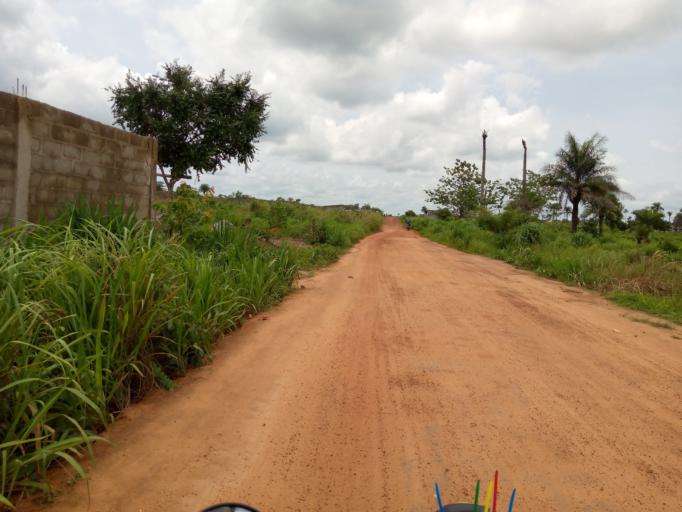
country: SL
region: Western Area
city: Waterloo
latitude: 8.3510
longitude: -12.9568
